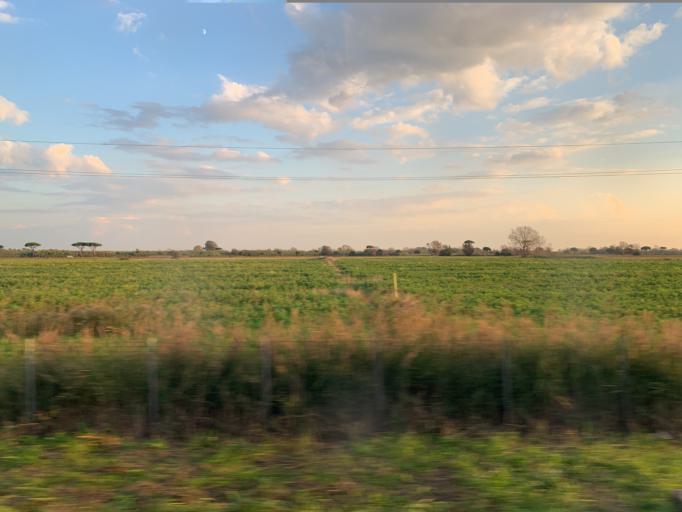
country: IT
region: Latium
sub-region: Citta metropolitana di Roma Capitale
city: Npp 23 (Parco Leonardo)
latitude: 41.7904
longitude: 12.2752
